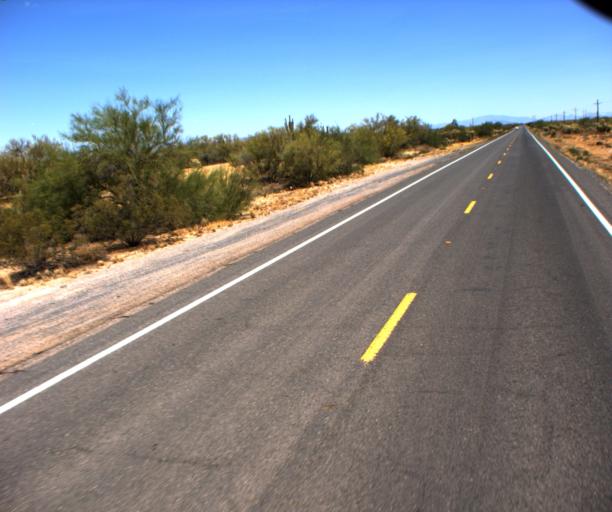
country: US
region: Arizona
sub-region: Pinal County
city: Florence
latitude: 32.9382
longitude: -111.3142
